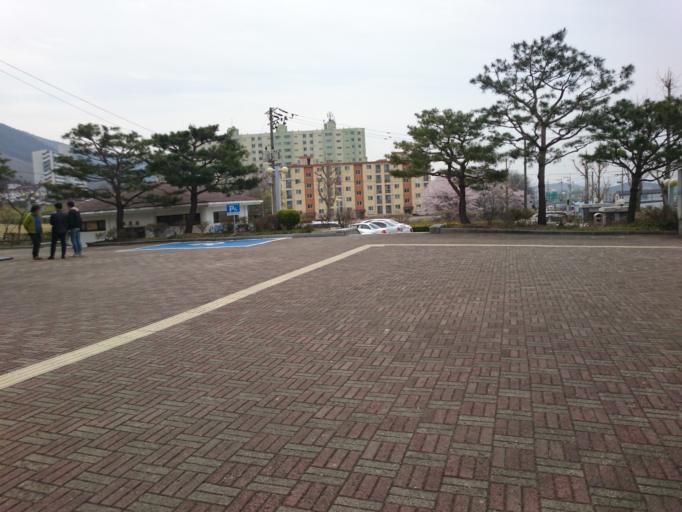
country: KR
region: Gyeongsangnam-do
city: Changnyeong
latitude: 35.5458
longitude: 128.5048
